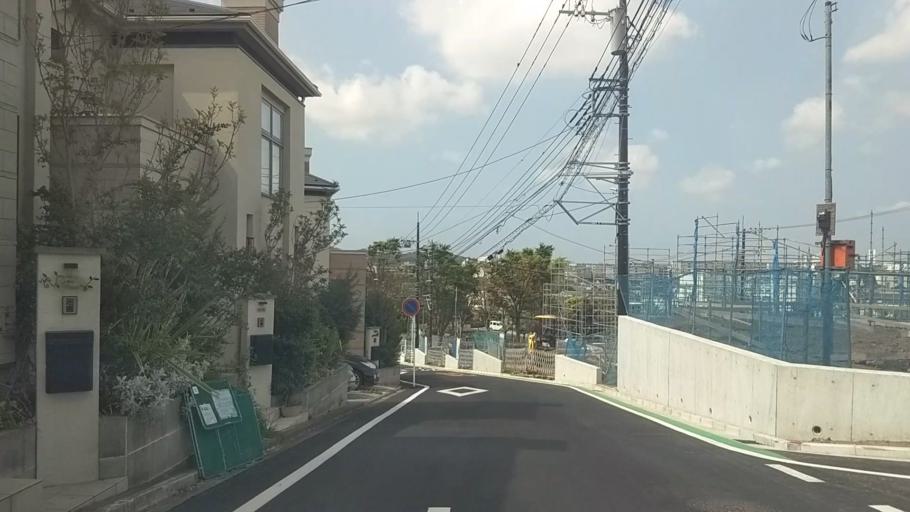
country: JP
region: Kanagawa
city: Yokohama
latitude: 35.3773
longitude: 139.6037
